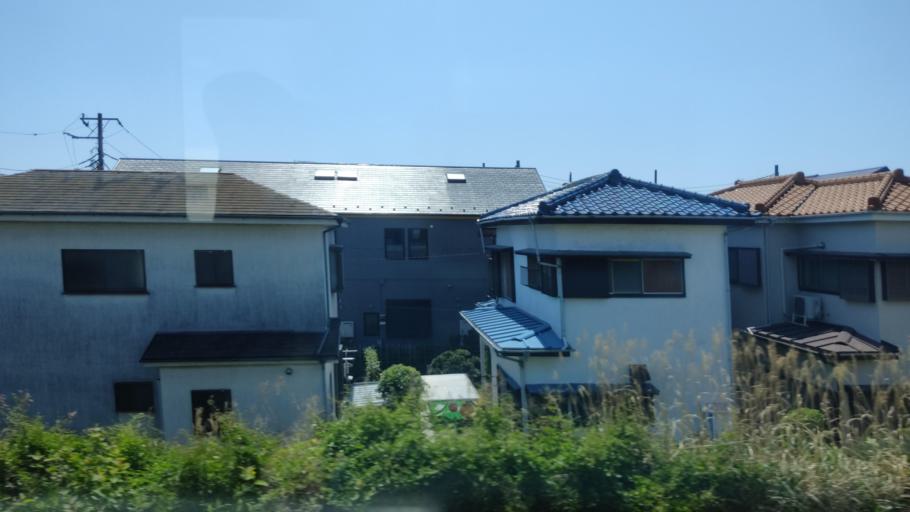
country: JP
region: Kanagawa
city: Chigasaki
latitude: 35.3284
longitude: 139.3872
